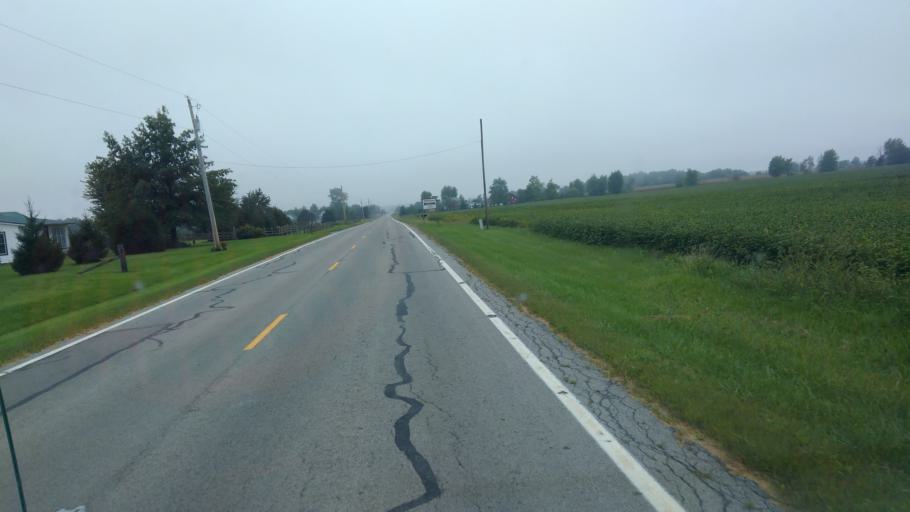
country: US
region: Ohio
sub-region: Hardin County
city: Kenton
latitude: 40.5254
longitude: -83.6035
